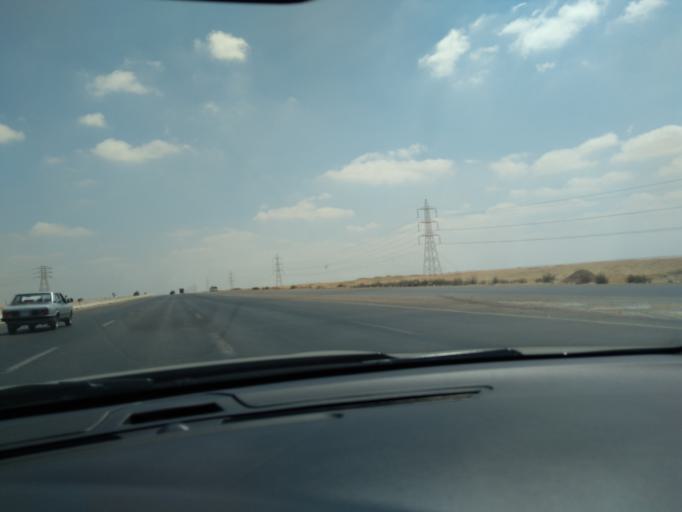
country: EG
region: Al Isma'iliyah
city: At Tall al Kabir
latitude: 30.3700
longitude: 31.9242
